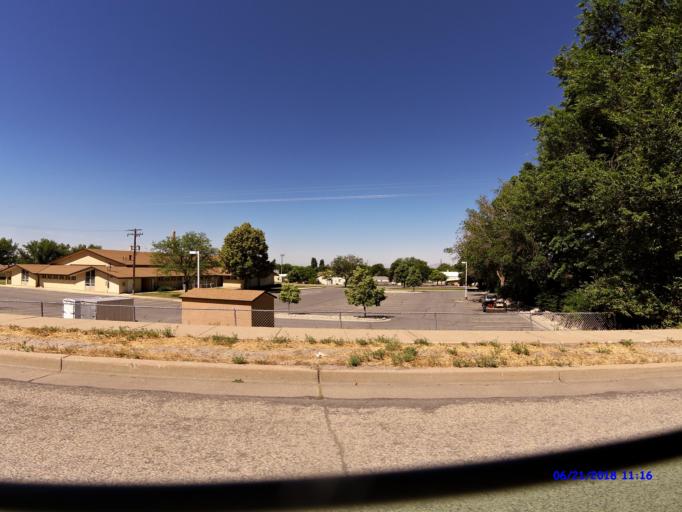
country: US
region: Utah
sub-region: Weber County
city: Harrisville
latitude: 41.2586
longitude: -111.9561
